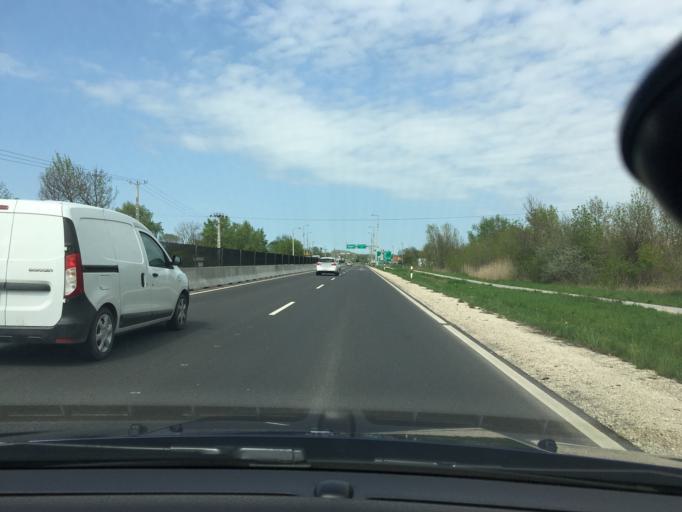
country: HU
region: Csongrad
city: Algyo
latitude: 46.3342
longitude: 20.1986
